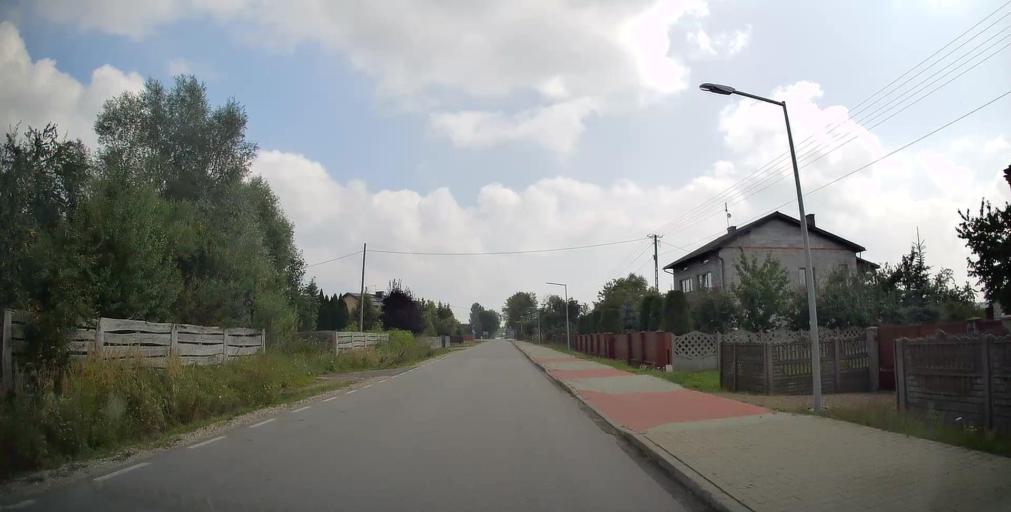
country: PL
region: Masovian Voivodeship
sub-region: Powiat bialobrzeski
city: Sucha
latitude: 51.6097
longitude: 20.9755
